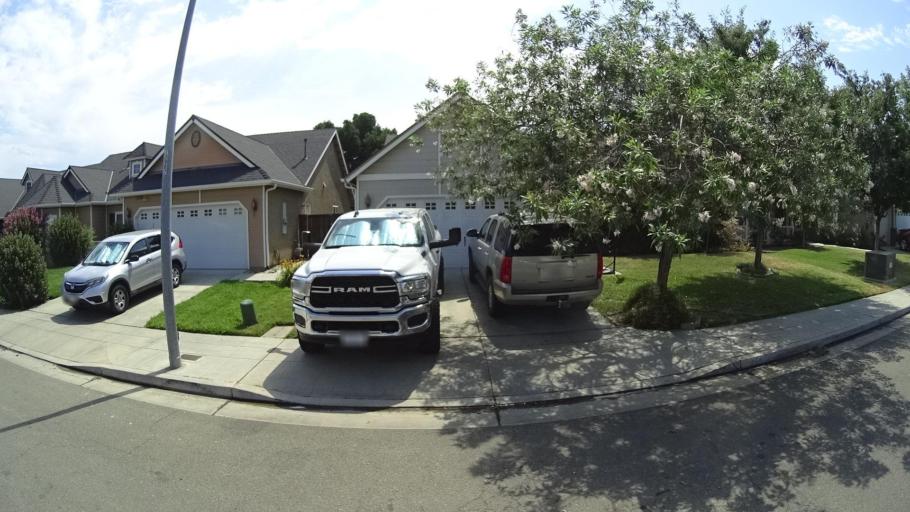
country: US
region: California
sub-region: Fresno County
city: Tarpey Village
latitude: 36.7818
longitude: -119.6665
